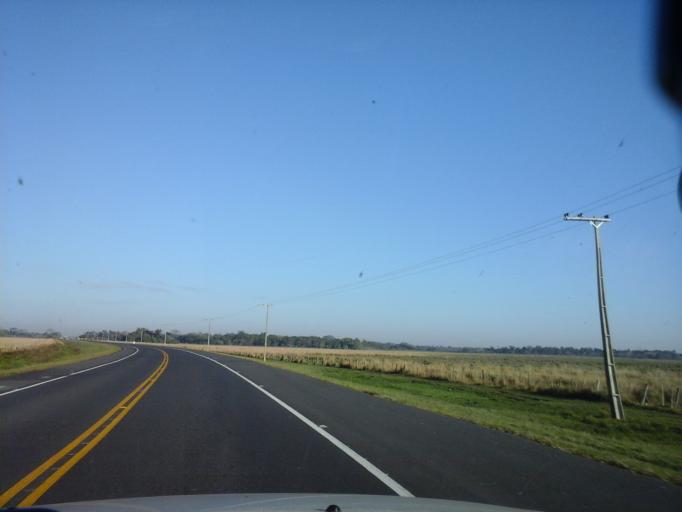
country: PY
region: Neembucu
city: Pilar
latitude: -26.8552
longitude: -57.9654
